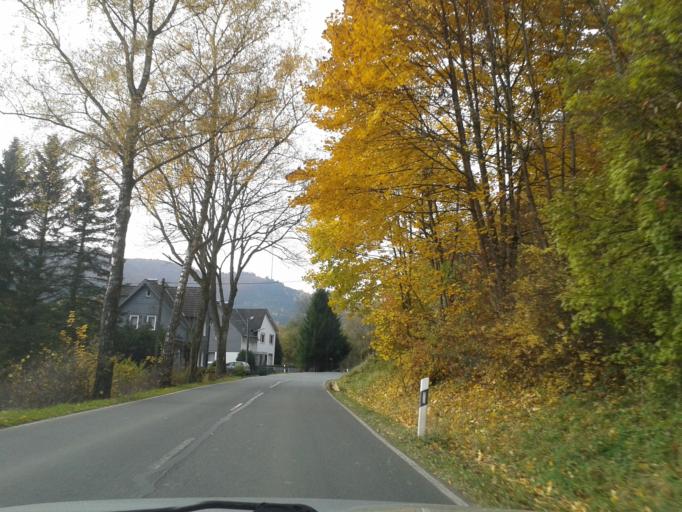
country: DE
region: North Rhine-Westphalia
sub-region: Regierungsbezirk Arnsberg
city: Bad Laasphe
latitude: 50.9205
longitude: 8.3990
